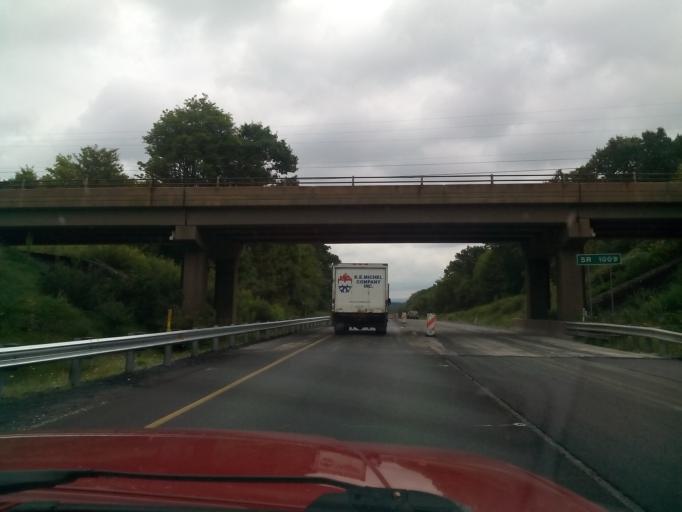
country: US
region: Pennsylvania
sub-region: Jefferson County
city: Reynoldsville
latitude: 41.1511
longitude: -78.8731
